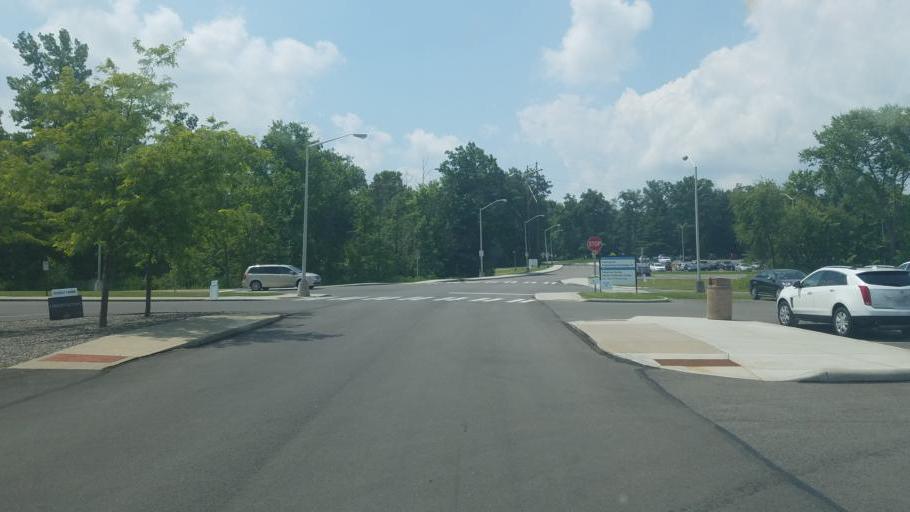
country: US
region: Ohio
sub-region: Richland County
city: Ontario
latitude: 40.7994
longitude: -82.5786
